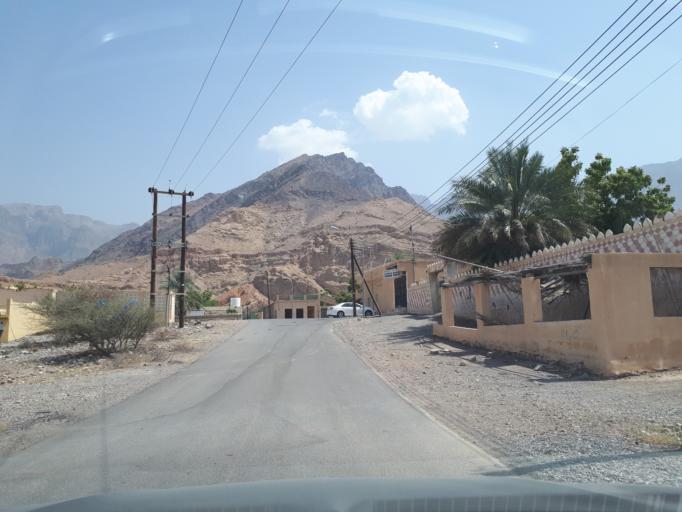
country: OM
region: Ash Sharqiyah
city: Ibra'
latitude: 23.0880
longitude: 58.8524
